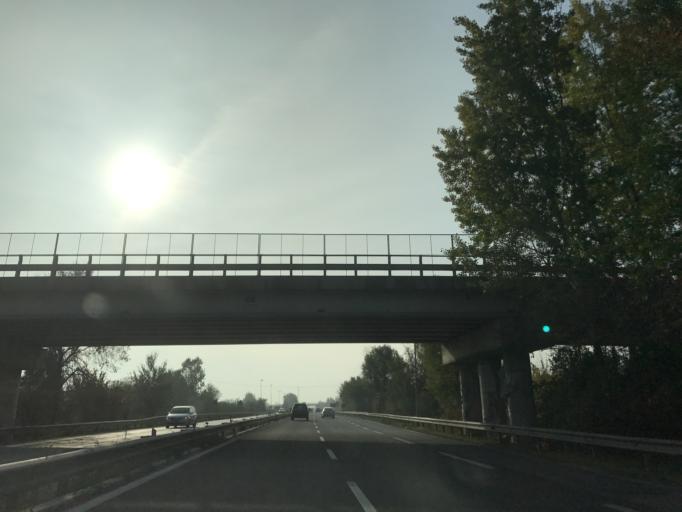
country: IT
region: Emilia-Romagna
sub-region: Provincia di Rimini
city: Bellaria-Igea Marina
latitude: 44.1425
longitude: 12.4571
